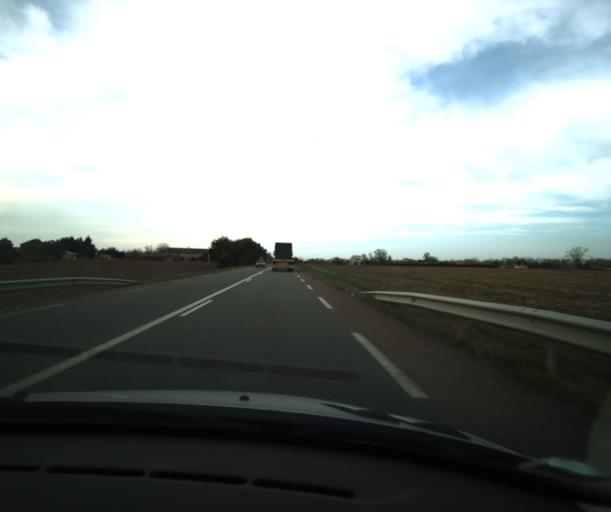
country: FR
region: Midi-Pyrenees
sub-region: Departement du Tarn-et-Garonne
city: Saint-Porquier
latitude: 43.9978
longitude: 1.1857
